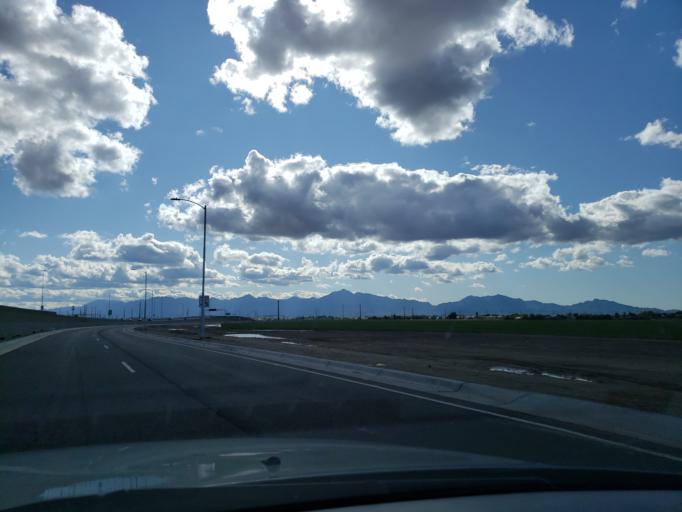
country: US
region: Arizona
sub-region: Maricopa County
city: Laveen
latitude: 33.4294
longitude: -112.1880
